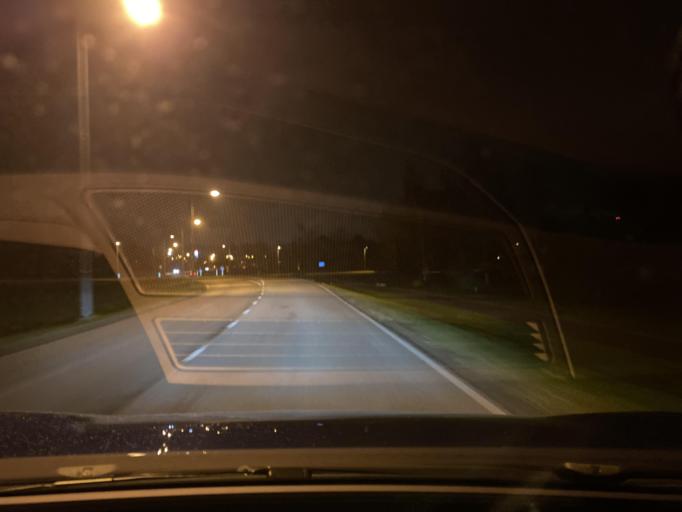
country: FI
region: Varsinais-Suomi
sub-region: Turku
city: Naantali
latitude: 60.4760
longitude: 22.0459
